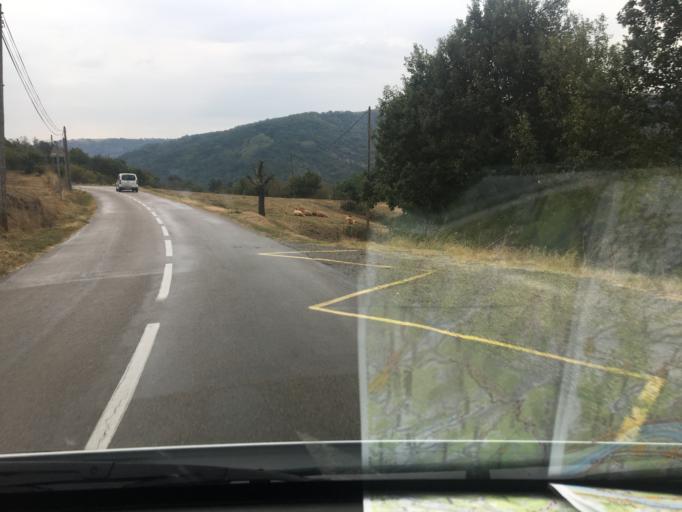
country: FR
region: Rhone-Alpes
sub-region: Departement de l'Ardeche
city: Saint-Felicien
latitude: 45.0540
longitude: 4.7076
